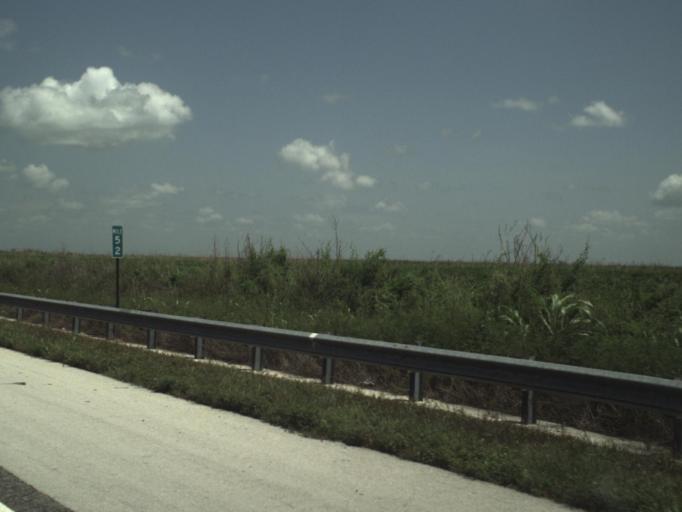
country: US
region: Florida
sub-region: Palm Beach County
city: Belle Glade Camp
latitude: 26.3899
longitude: -80.5802
